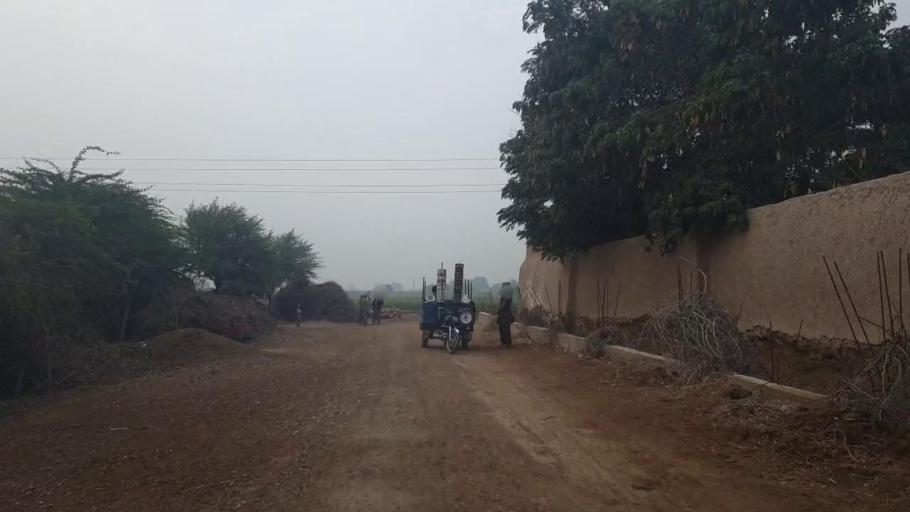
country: PK
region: Sindh
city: Tando Adam
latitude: 25.6929
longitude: 68.6575
